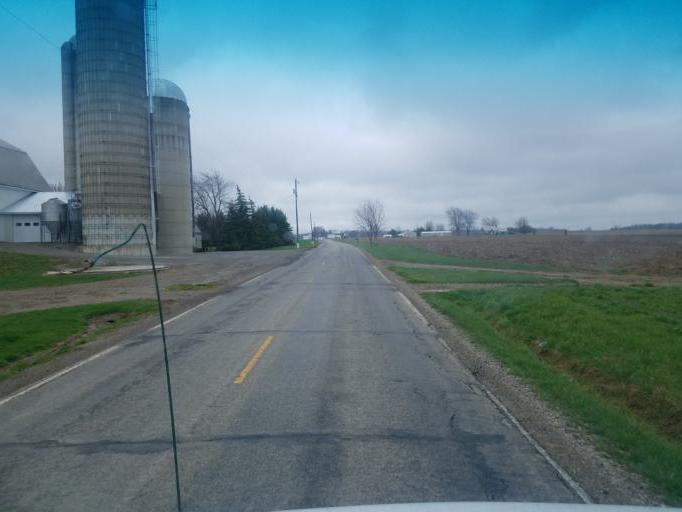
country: US
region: Ohio
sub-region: Richland County
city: Shelby
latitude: 40.9333
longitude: -82.6440
